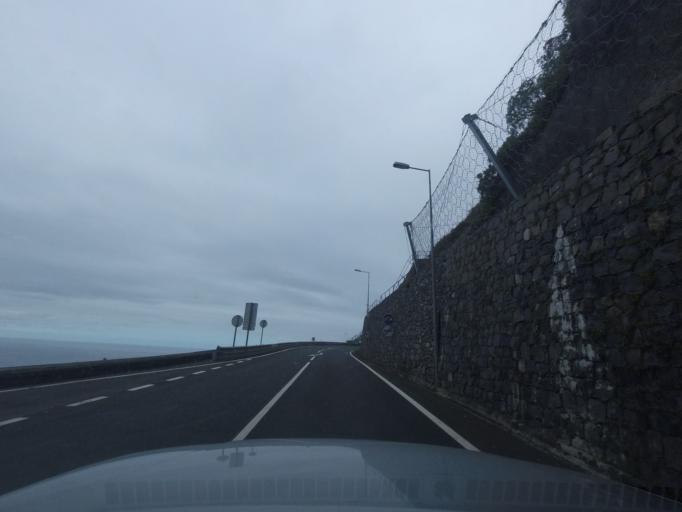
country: PT
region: Madeira
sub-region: Porto Moniz
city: Porto Moniz
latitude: 32.8593
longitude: -17.1615
